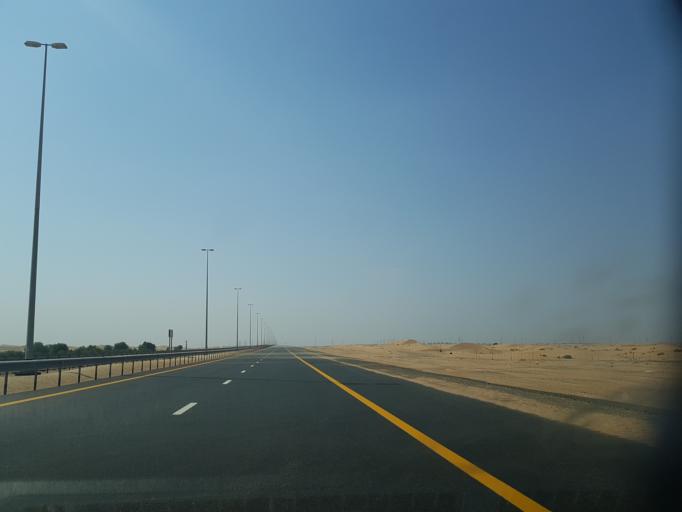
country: AE
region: Ash Shariqah
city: Sharjah
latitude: 25.2758
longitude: 55.6177
